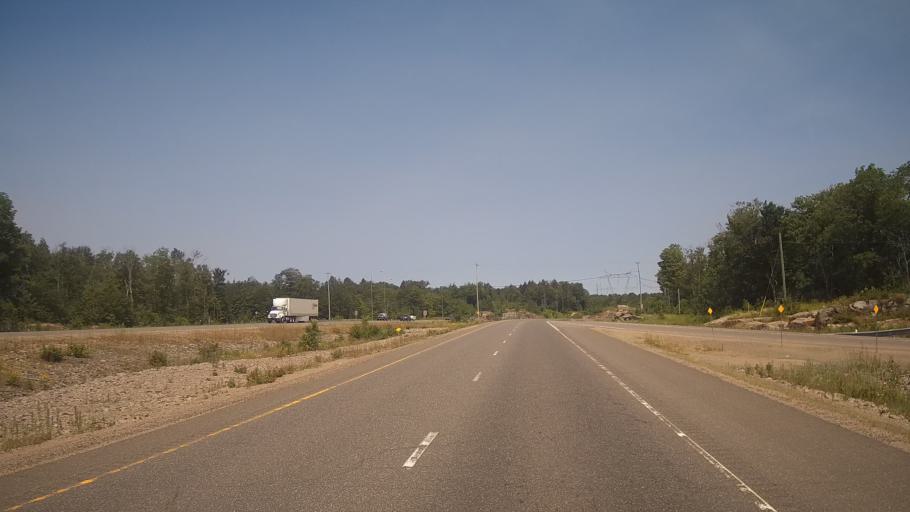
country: CA
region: Ontario
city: Midland
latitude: 45.0576
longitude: -79.7855
